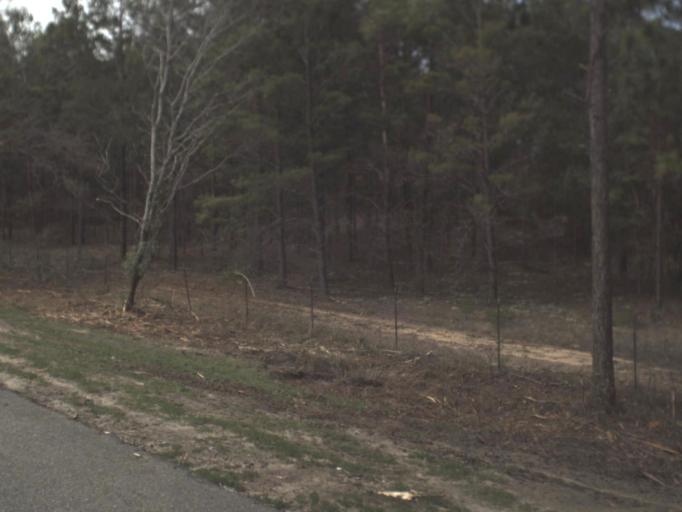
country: US
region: Florida
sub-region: Liberty County
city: Bristol
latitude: 30.4920
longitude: -84.9000
